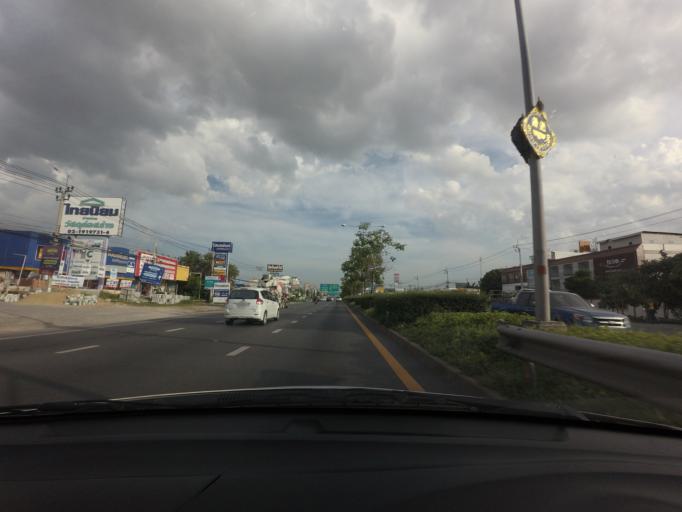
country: TH
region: Nonthaburi
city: Bang Bua Thong
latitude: 13.8874
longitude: 100.4504
